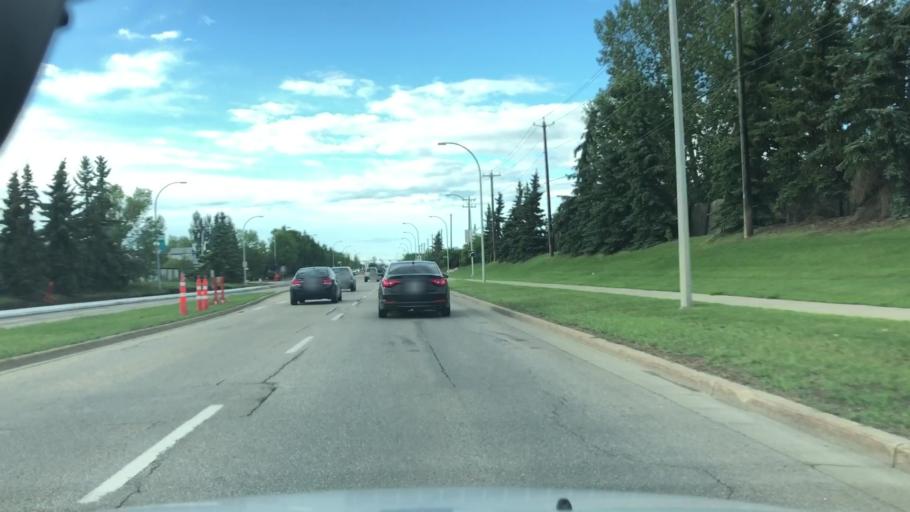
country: CA
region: Alberta
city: St. Albert
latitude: 53.6189
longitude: -113.5411
